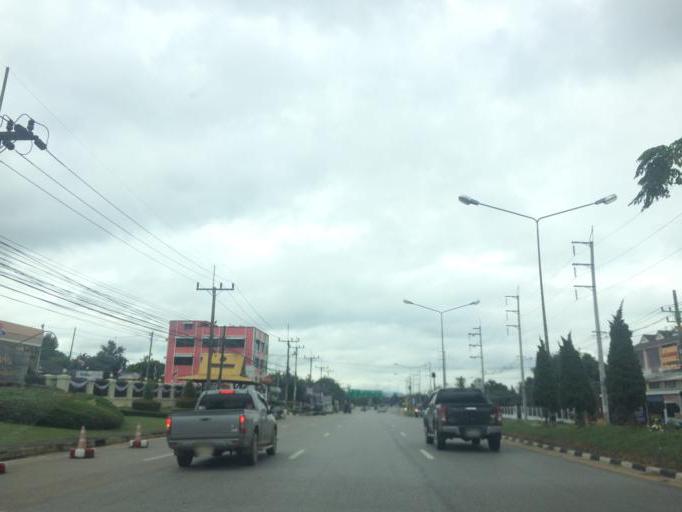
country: TH
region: Chiang Rai
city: Mae Chan
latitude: 20.1347
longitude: 99.8605
